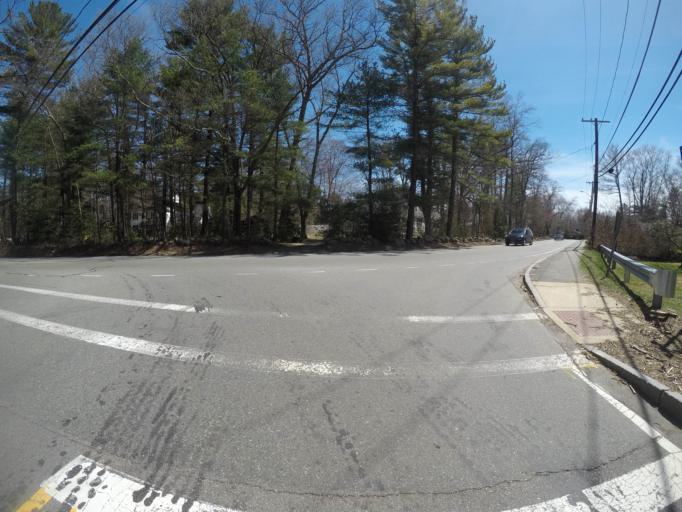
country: US
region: Massachusetts
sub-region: Bristol County
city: Easton
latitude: 42.0416
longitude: -71.0900
